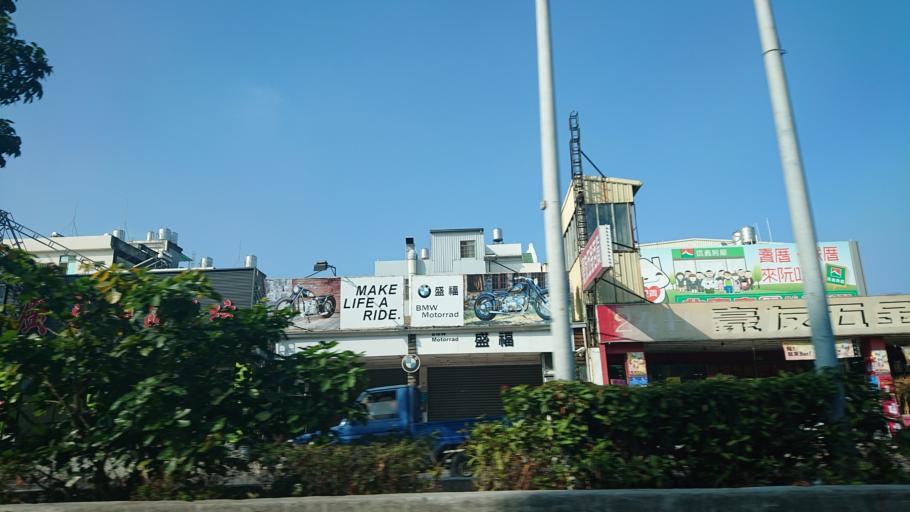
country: TW
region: Taiwan
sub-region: Tainan
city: Tainan
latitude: 23.0096
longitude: 120.1855
